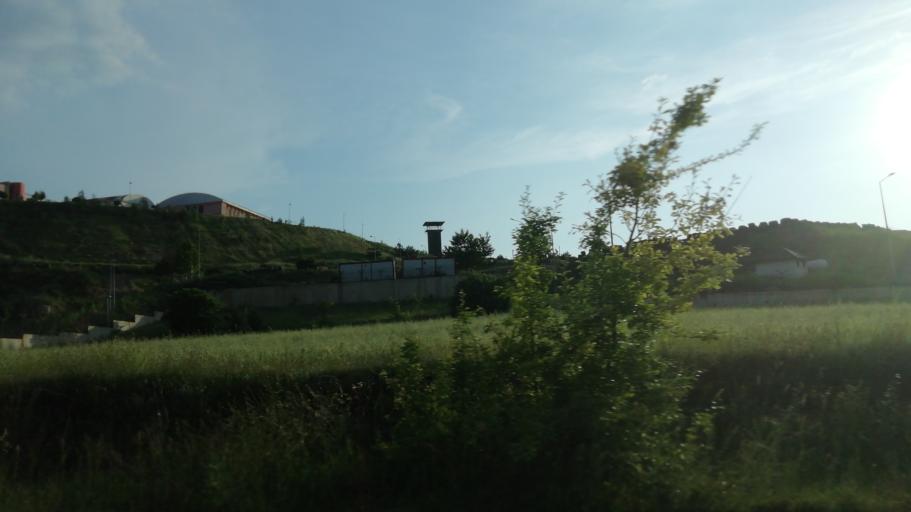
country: TR
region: Karabuk
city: Karabuk
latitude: 41.1374
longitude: 32.6317
